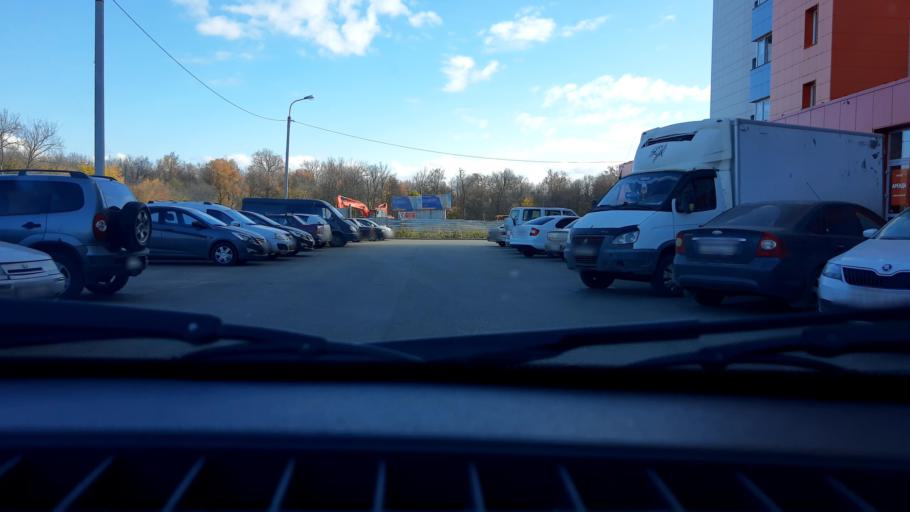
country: RU
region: Bashkortostan
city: Ufa
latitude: 54.7794
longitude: 56.1353
